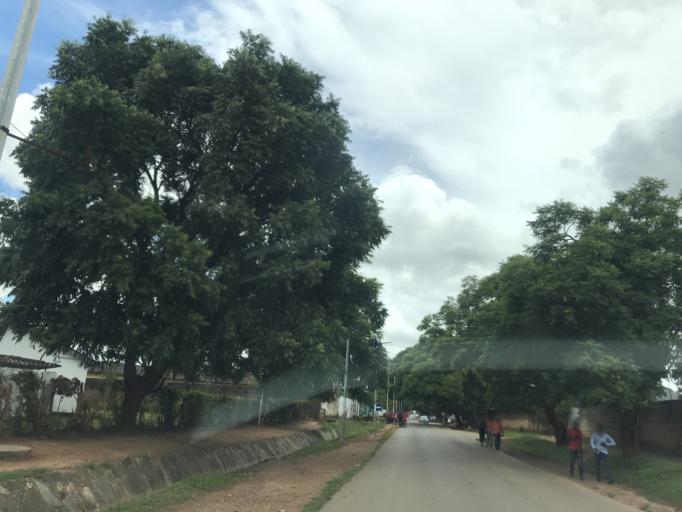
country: ZM
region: Lusaka
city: Lusaka
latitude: -15.4308
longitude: 28.3050
